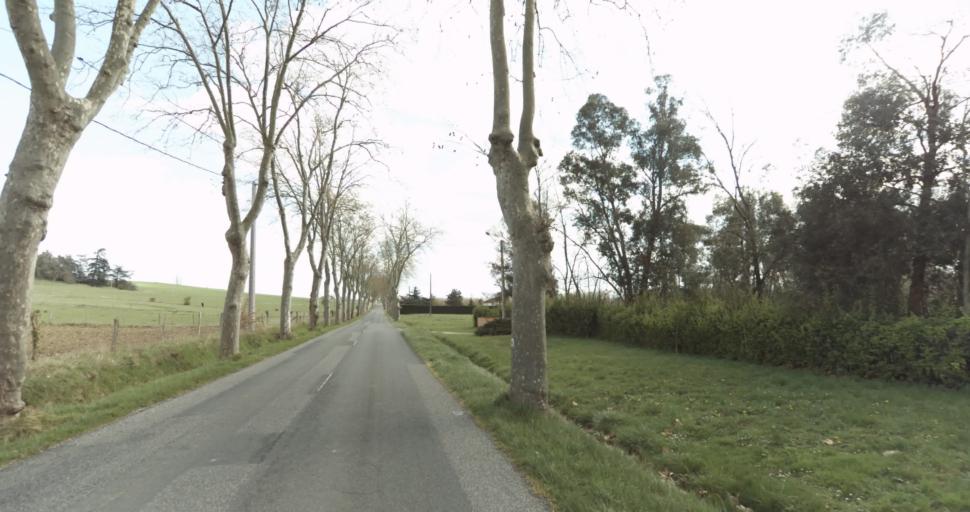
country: FR
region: Midi-Pyrenees
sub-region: Departement de la Haute-Garonne
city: Auterive
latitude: 43.3721
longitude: 1.4683
